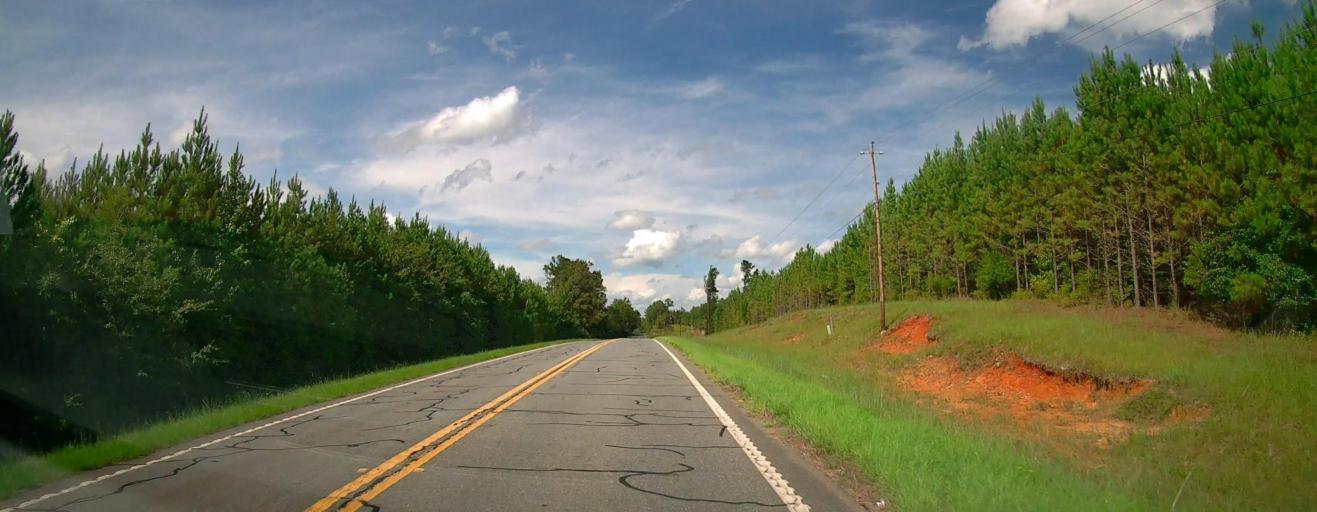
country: US
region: Georgia
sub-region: Talbot County
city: Talbotton
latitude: 32.7266
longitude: -84.5554
